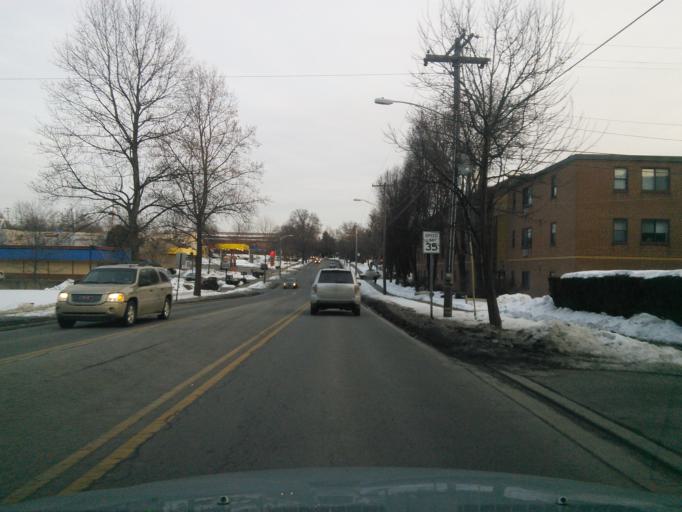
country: US
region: Pennsylvania
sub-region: Centre County
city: State College
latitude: 40.8002
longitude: -77.8493
